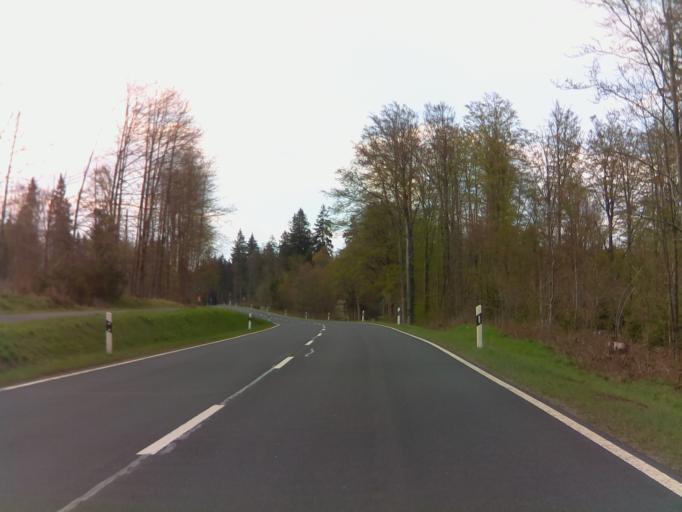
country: DE
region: Bavaria
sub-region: Upper Franconia
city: Ludwigsstadt
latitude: 50.4551
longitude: 11.3490
